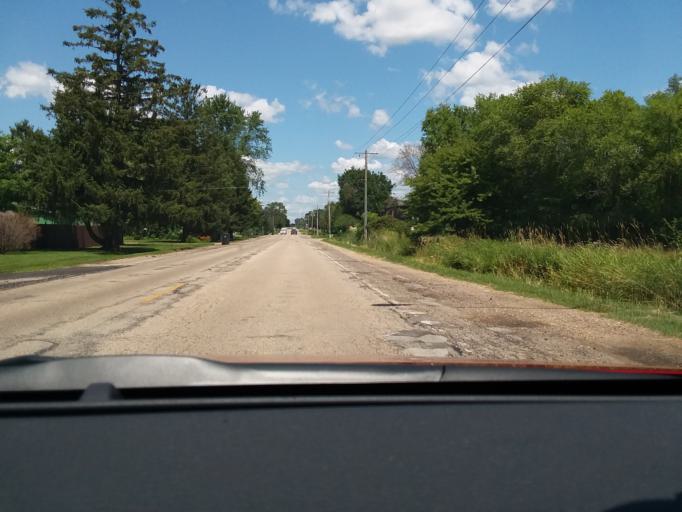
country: US
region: Wisconsin
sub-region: Dane County
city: Windsor
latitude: 43.2032
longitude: -89.3430
